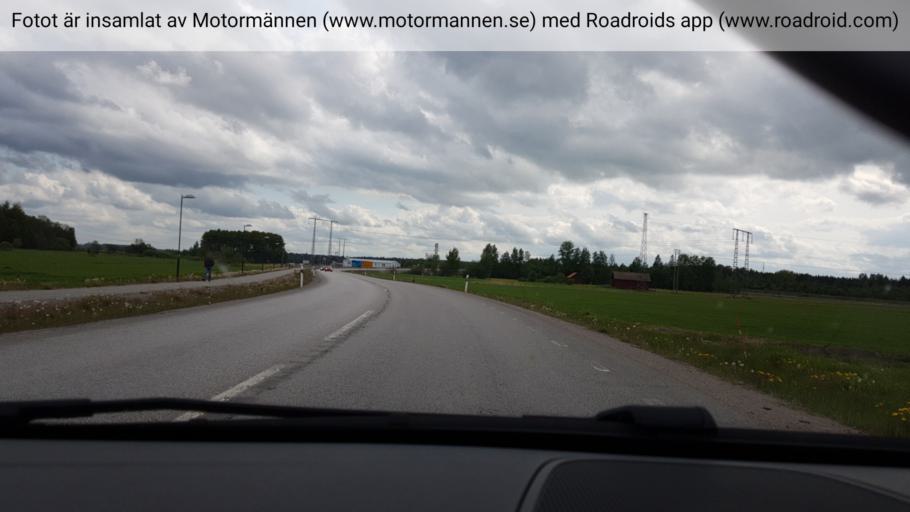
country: SE
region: Uppsala
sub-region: Tierps Kommun
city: Tierp
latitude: 60.3452
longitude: 17.4901
